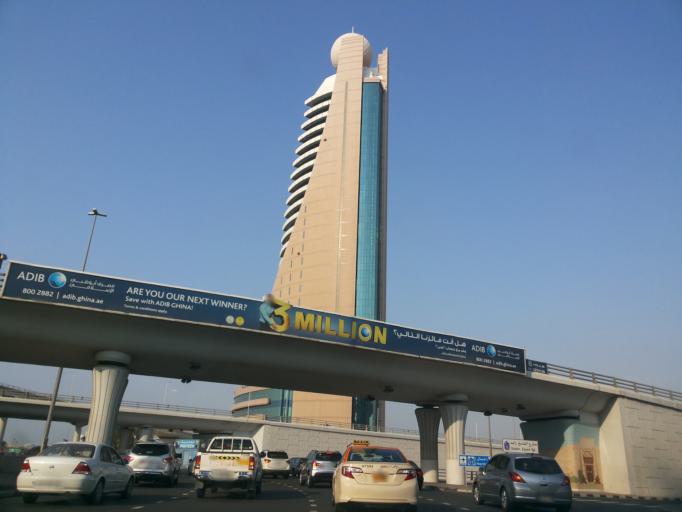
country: AE
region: Ash Shariqah
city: Sharjah
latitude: 25.2292
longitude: 55.2908
